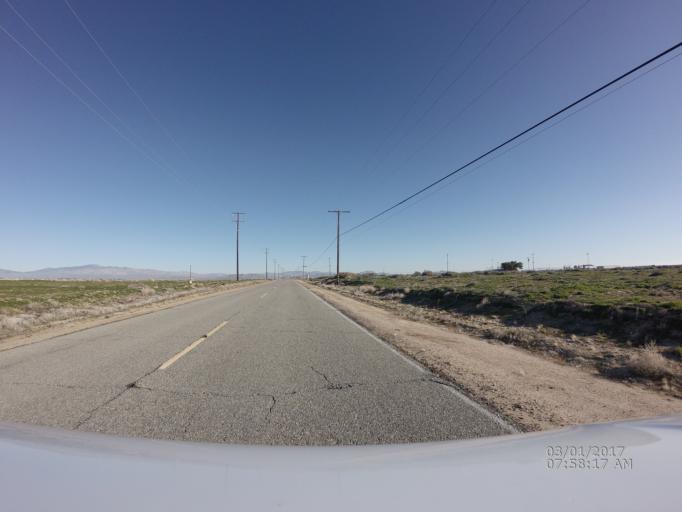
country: US
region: California
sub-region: Kern County
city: Rosamond
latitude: 34.7718
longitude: -118.2549
